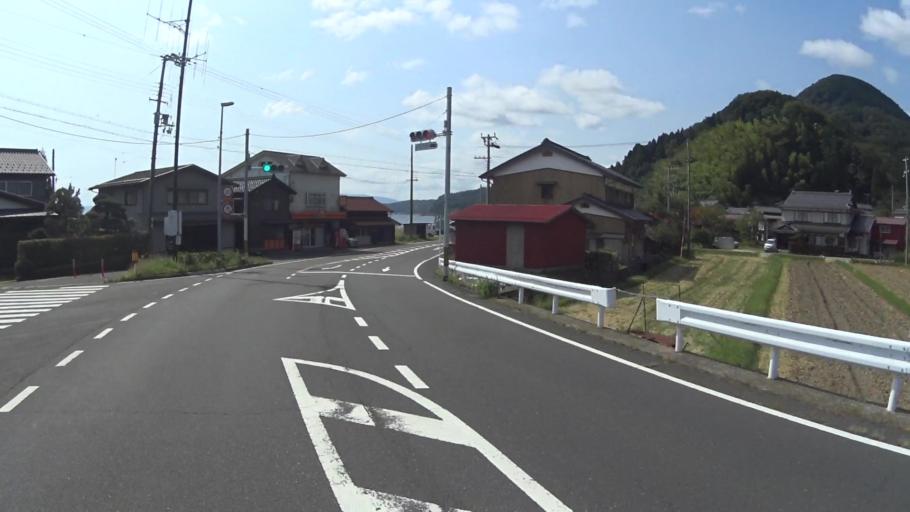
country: JP
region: Kyoto
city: Miyazu
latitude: 35.6563
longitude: 135.2590
